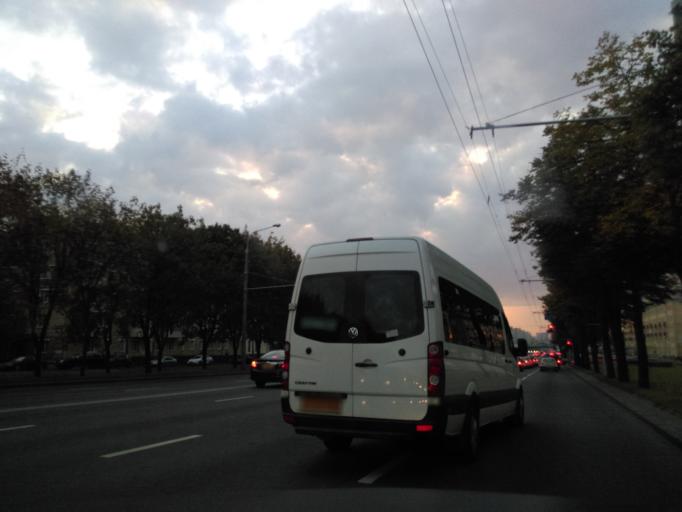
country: BY
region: Minsk
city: Minsk
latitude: 53.8737
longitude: 27.6353
